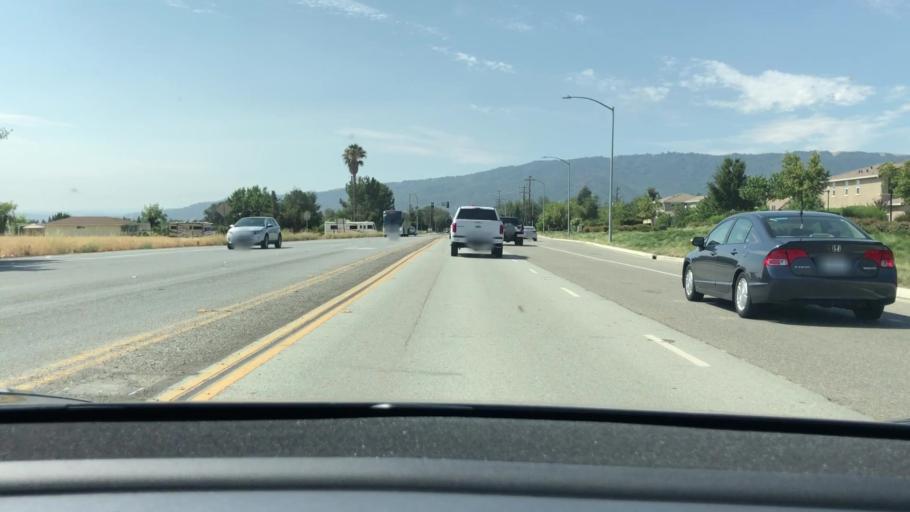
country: US
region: California
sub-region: Santa Clara County
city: Gilroy
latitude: 37.0350
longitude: -121.5975
